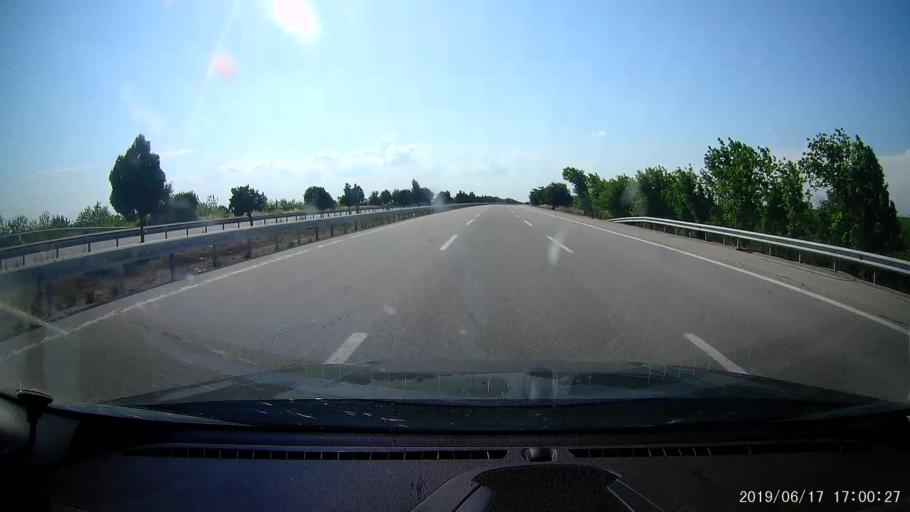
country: TR
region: Edirne
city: Haskoy
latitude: 41.6208
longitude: 26.8306
